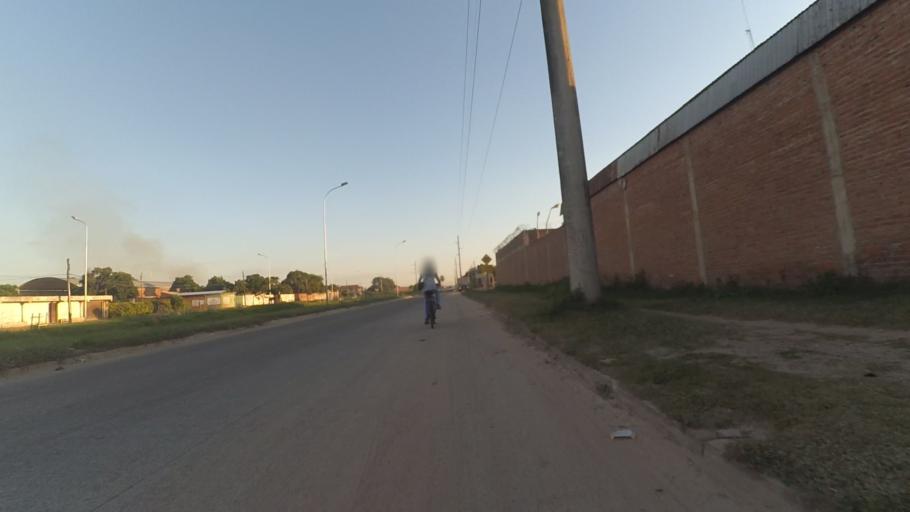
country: BO
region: Santa Cruz
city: Cotoca
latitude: -17.7723
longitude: -63.1077
